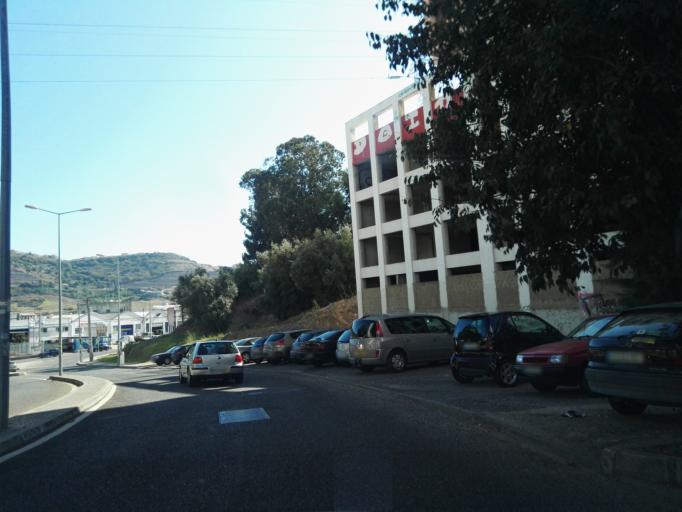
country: PT
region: Lisbon
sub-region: Odivelas
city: Povoa de Santo Adriao
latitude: 38.8069
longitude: -9.1584
